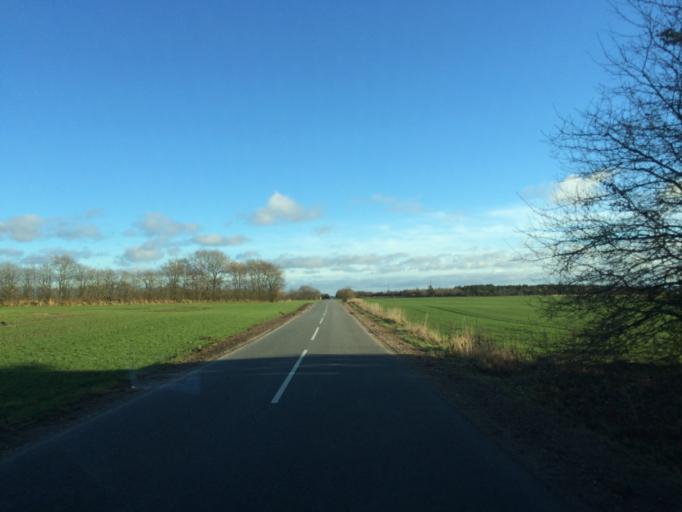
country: DK
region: Central Jutland
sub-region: Herning Kommune
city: Kibaek
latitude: 56.0423
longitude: 8.8261
